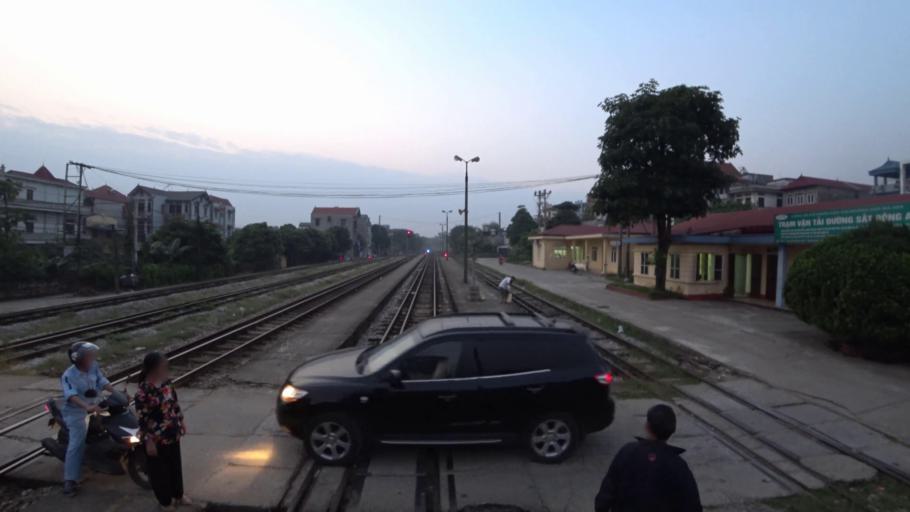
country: VN
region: Ha Noi
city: Soc Son
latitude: 21.2339
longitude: 105.8612
